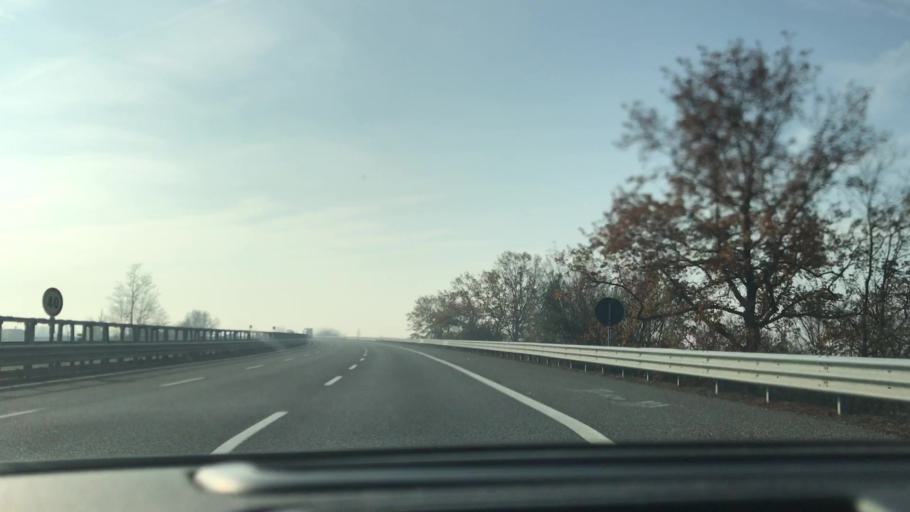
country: IT
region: Piedmont
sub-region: Provincia di Alessandria
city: Alessandria
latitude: 44.9025
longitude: 8.5690
